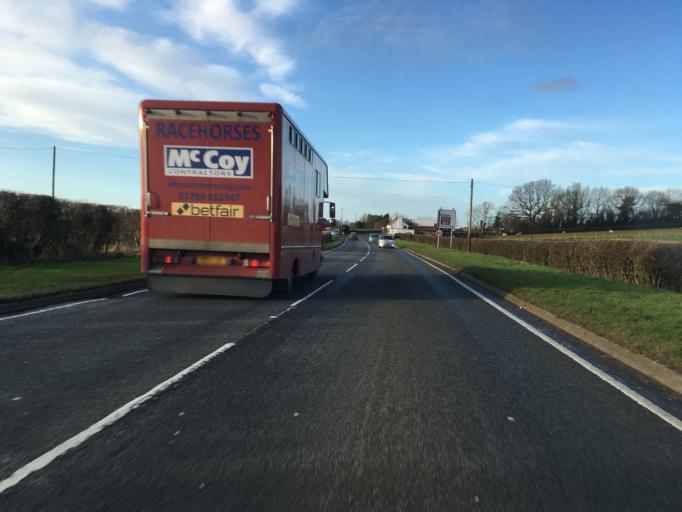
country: GB
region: England
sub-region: Warwickshire
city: Stratford-upon-Avon
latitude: 52.2218
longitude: -1.7340
